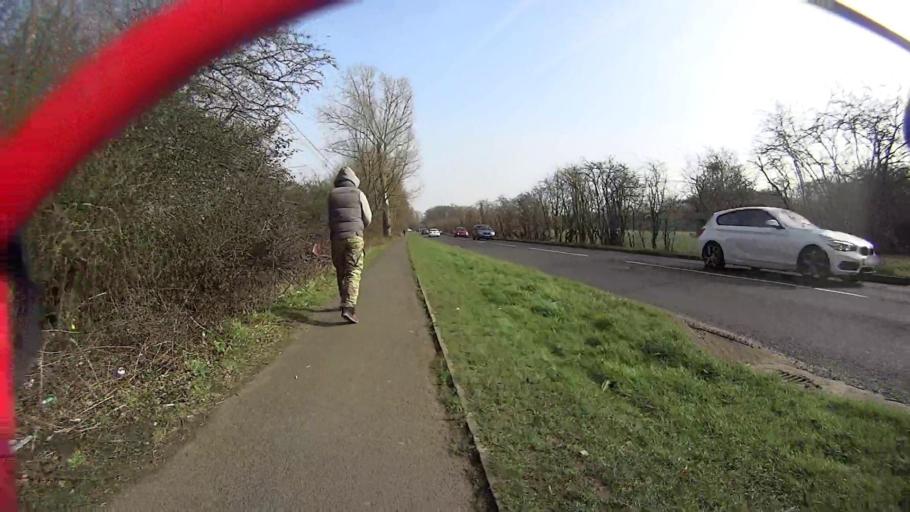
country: GB
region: England
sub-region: Surrey
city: Salfords
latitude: 51.2191
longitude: -0.1820
